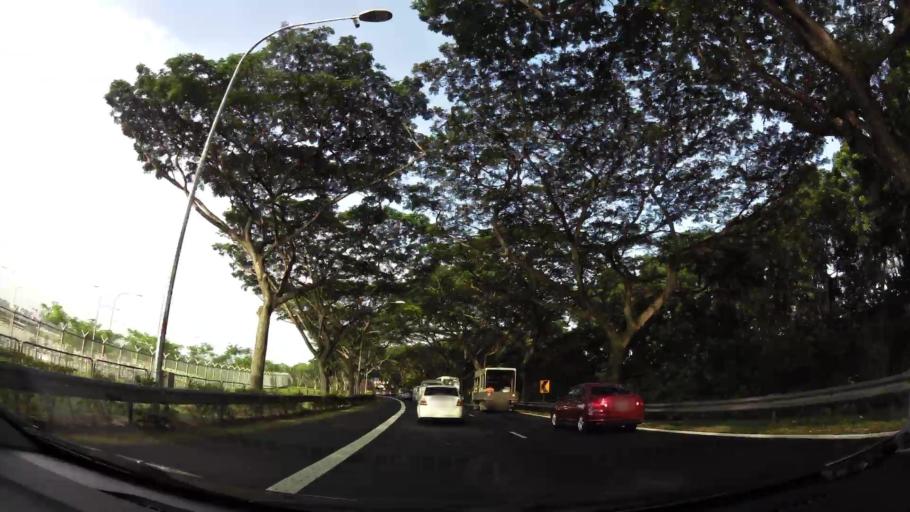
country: MY
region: Johor
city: Johor Bahru
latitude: 1.3626
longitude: 103.7071
